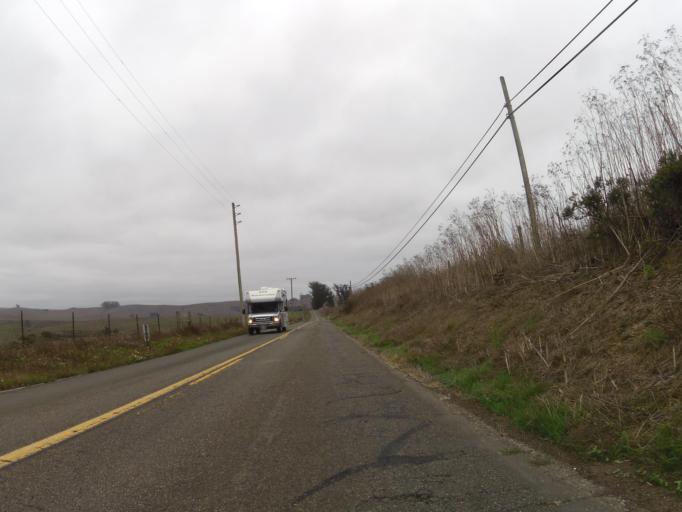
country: US
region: California
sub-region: Sonoma County
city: Occidental
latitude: 38.2857
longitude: -122.8993
